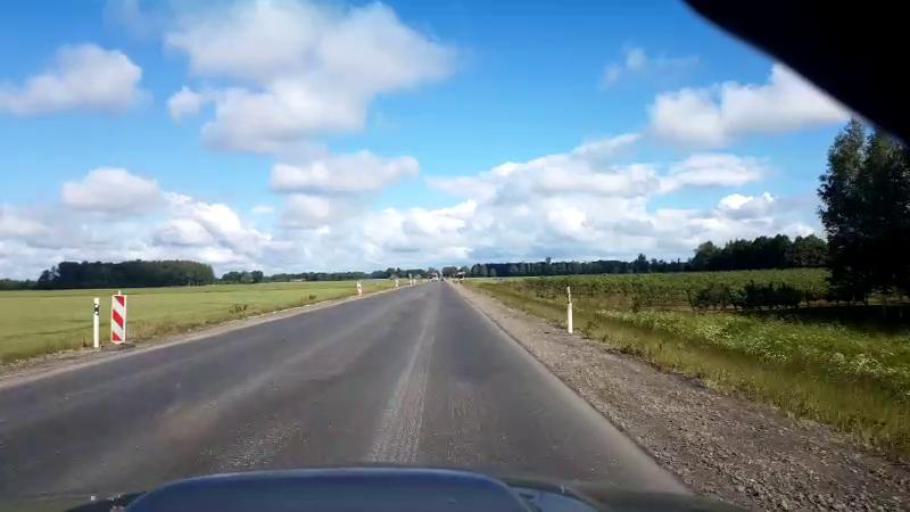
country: LV
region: Bauskas Rajons
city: Bauska
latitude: 56.3703
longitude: 24.2727
